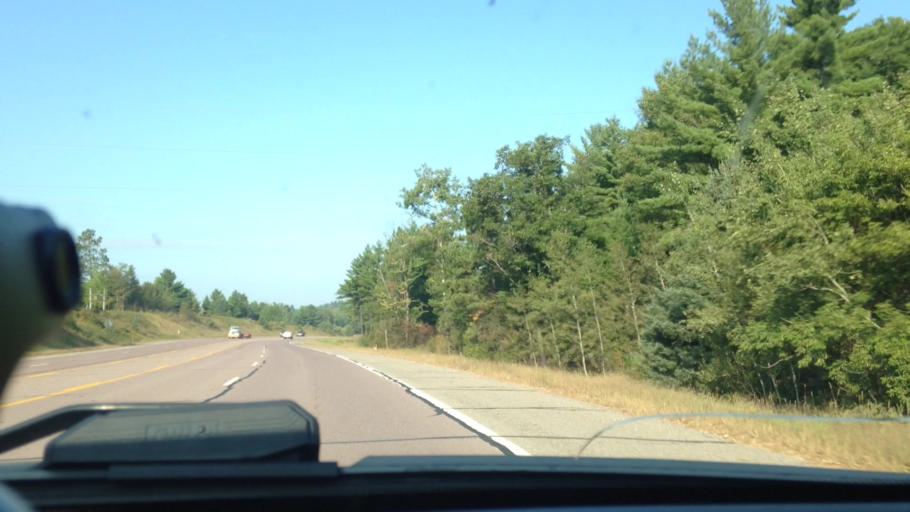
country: US
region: Michigan
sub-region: Dickinson County
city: Quinnesec
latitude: 45.8043
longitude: -87.9701
